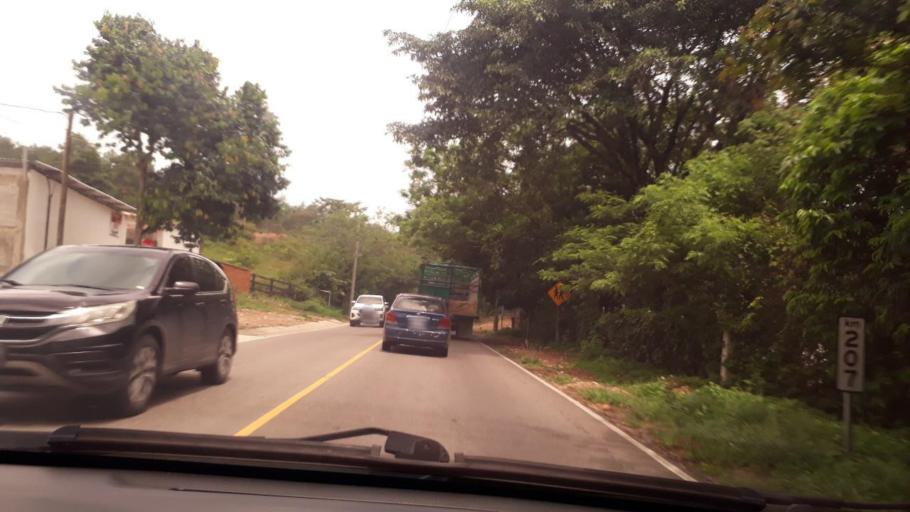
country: GT
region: Chiquimula
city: Concepcion Las Minas
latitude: 14.5661
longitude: -89.4500
